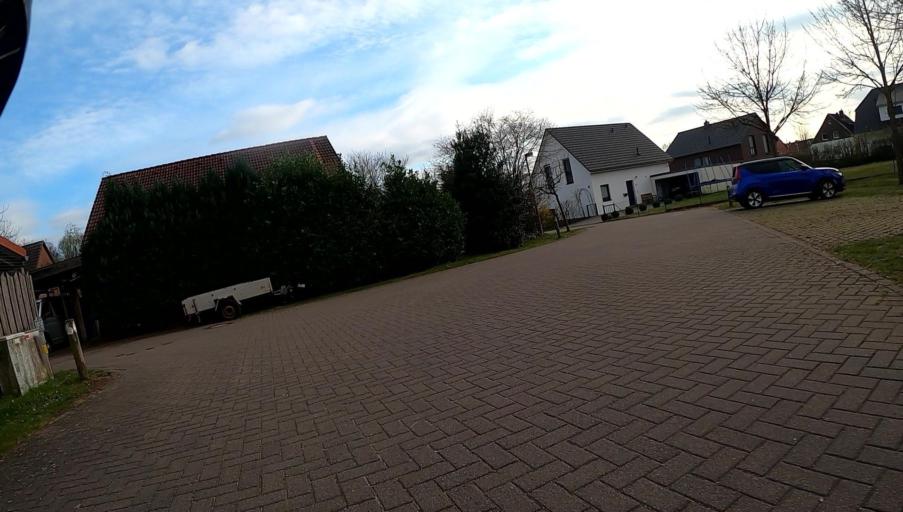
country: DE
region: Lower Saxony
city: Lindwedel
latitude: 52.5560
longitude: 9.6356
